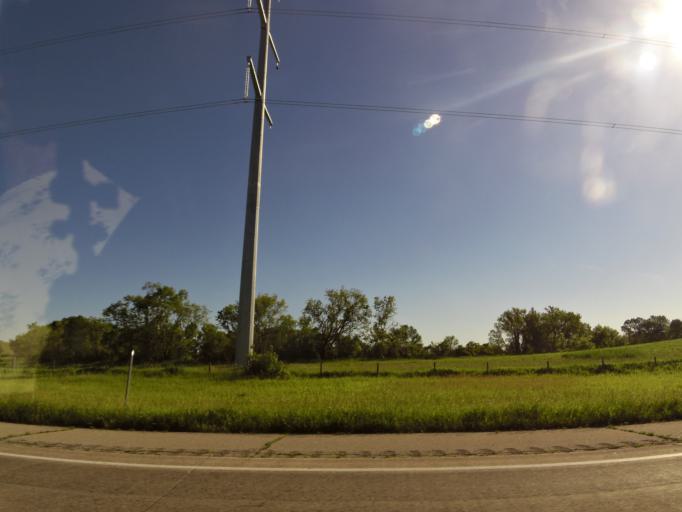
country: US
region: Minnesota
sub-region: Douglas County
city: Alexandria
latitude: 45.9216
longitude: -95.5612
